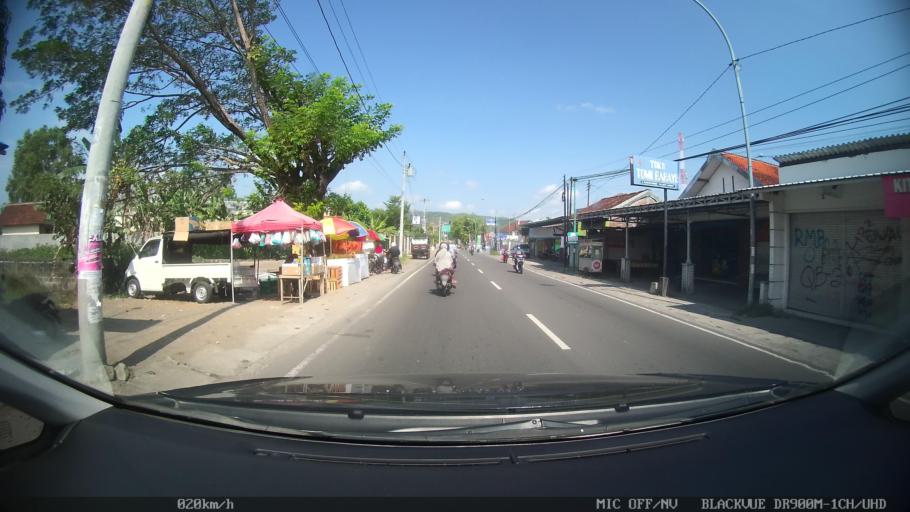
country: ID
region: Daerah Istimewa Yogyakarta
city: Pundong
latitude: -7.9188
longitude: 110.3791
